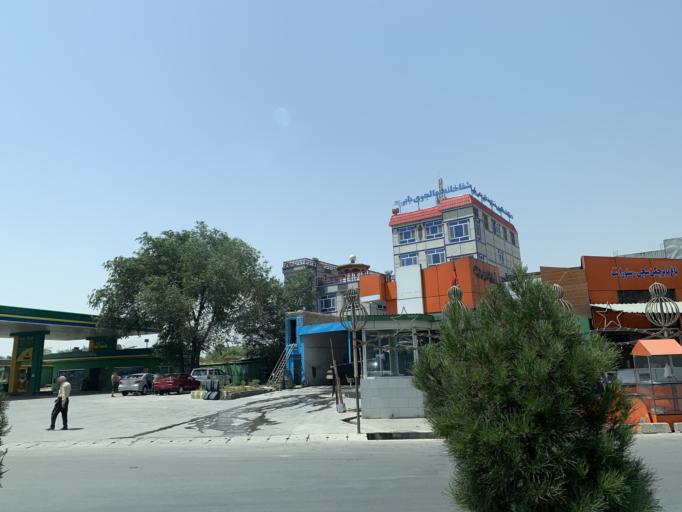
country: AF
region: Kabul
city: Kabul
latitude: 34.5008
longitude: 69.1566
